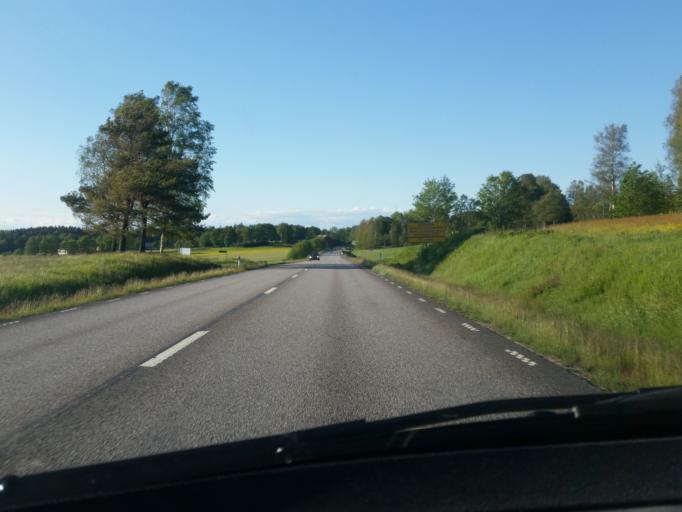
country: SE
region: Vaestra Goetaland
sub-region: Fargelanda Kommun
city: Faergelanda
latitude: 58.5440
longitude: 11.9891
